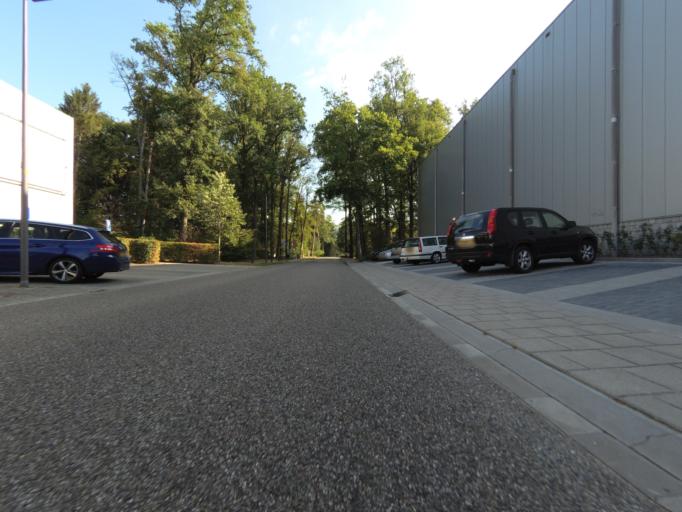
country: NL
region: Overijssel
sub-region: Gemeente Enschede
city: Enschede
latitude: 52.2442
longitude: 6.8496
